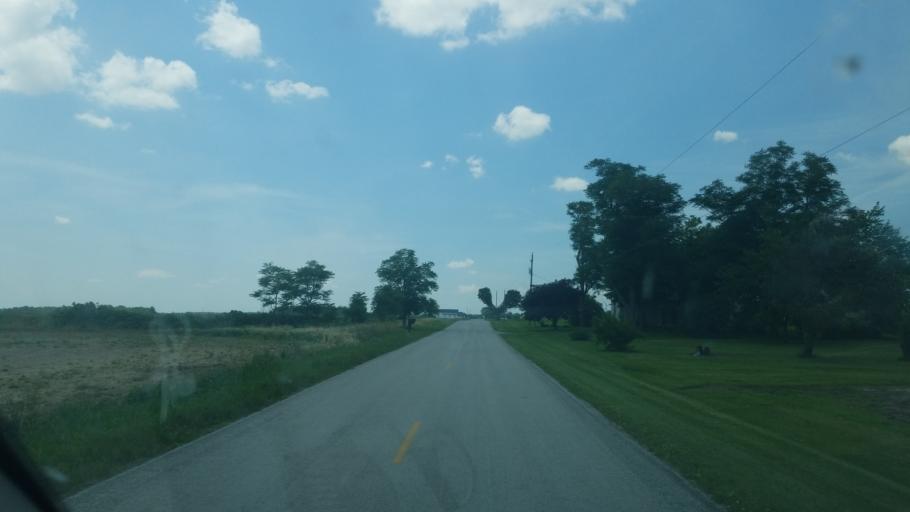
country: US
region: Ohio
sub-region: Hardin County
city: Forest
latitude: 40.7897
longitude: -83.6076
